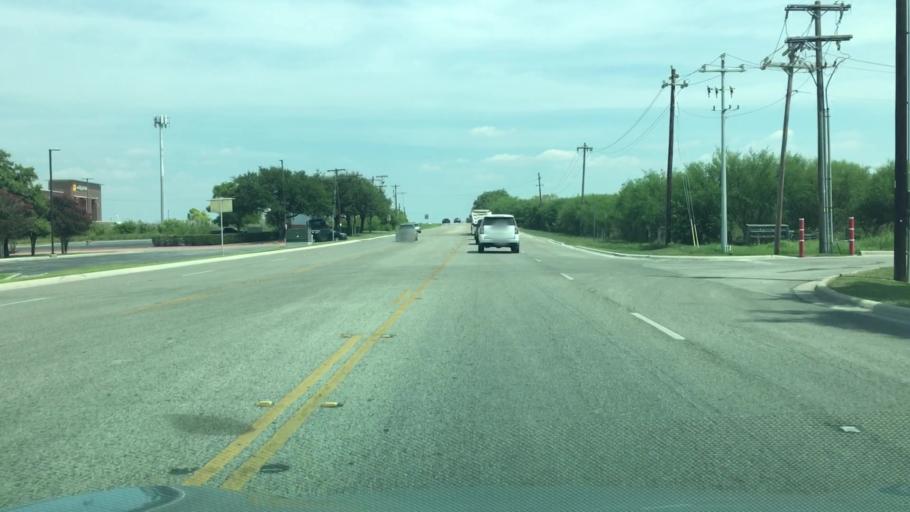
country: US
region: Texas
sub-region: Hays County
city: San Marcos
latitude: 29.8259
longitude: -97.9834
